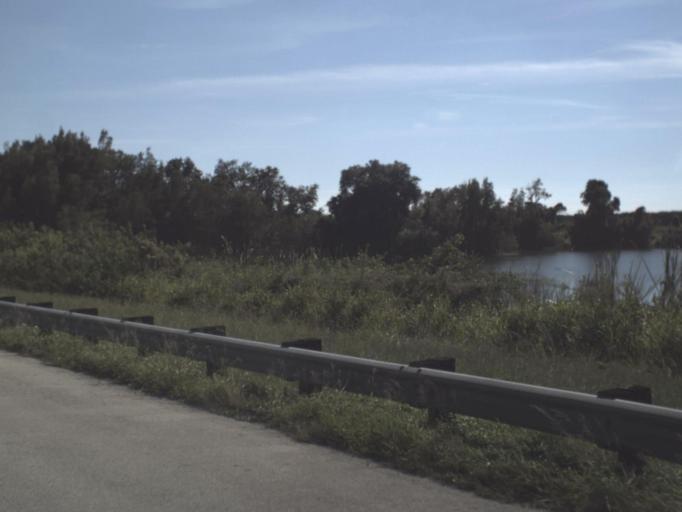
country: US
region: Florida
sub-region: Highlands County
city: Lake Placid
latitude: 27.2529
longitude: -81.3407
